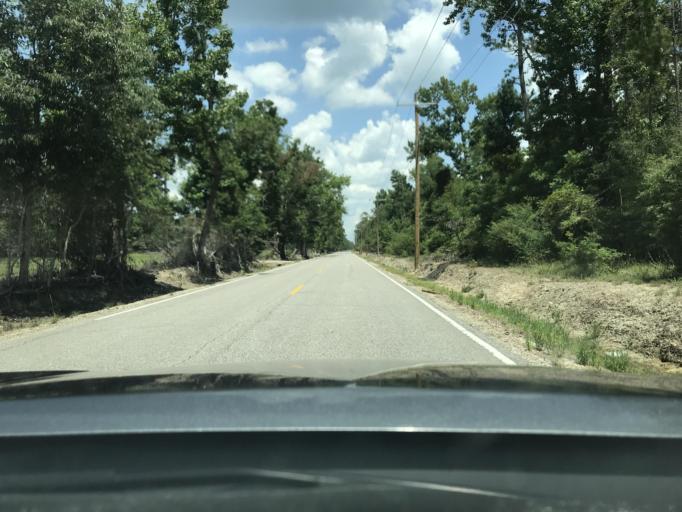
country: US
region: Louisiana
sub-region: Calcasieu Parish
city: Moss Bluff
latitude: 30.3300
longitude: -93.1632
